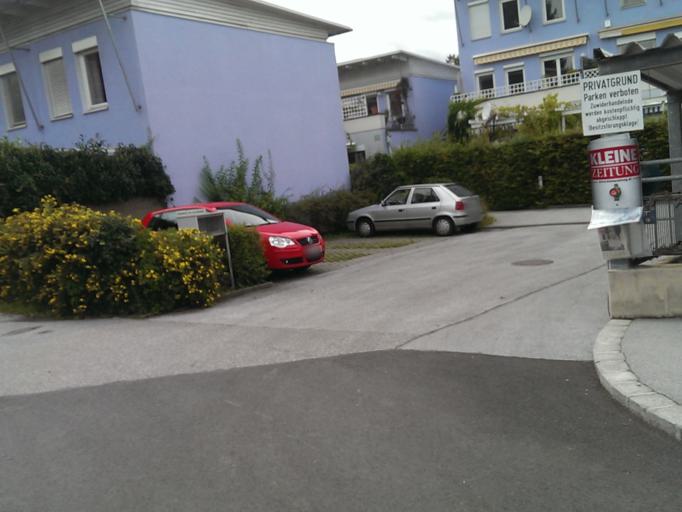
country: AT
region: Styria
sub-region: Graz Stadt
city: Graz
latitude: 47.0504
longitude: 15.4689
